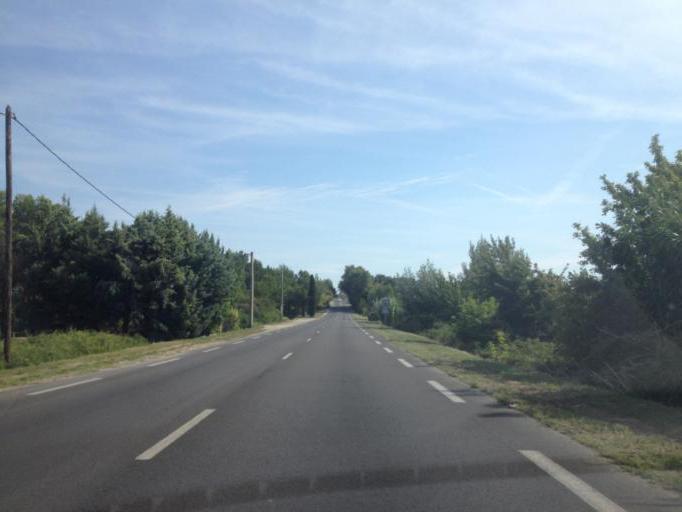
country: FR
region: Provence-Alpes-Cote d'Azur
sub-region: Departement du Vaucluse
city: Beaumes-de-Venise
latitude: 44.1111
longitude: 5.0198
